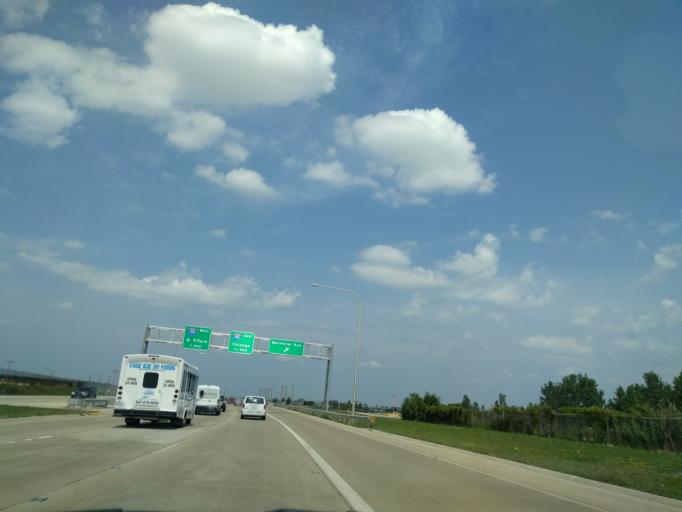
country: US
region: Illinois
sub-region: Cook County
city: Schiller Park
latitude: 41.9676
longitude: -87.8762
